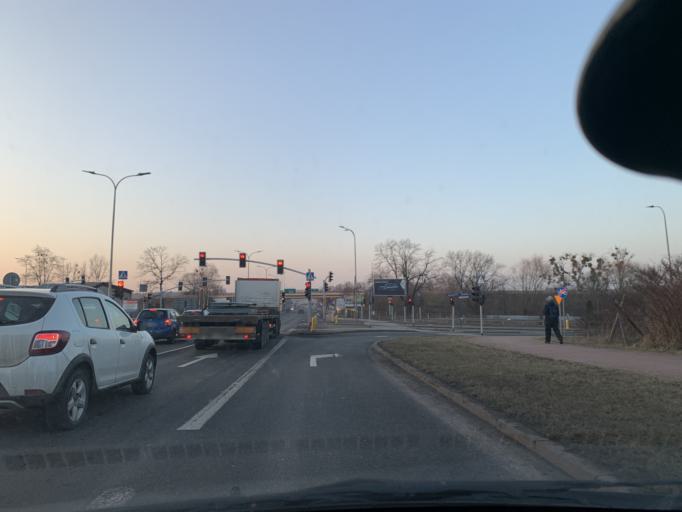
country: PL
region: Silesian Voivodeship
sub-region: Piekary Slaskie
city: Piekary Slaskie
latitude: 50.3670
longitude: 18.8984
